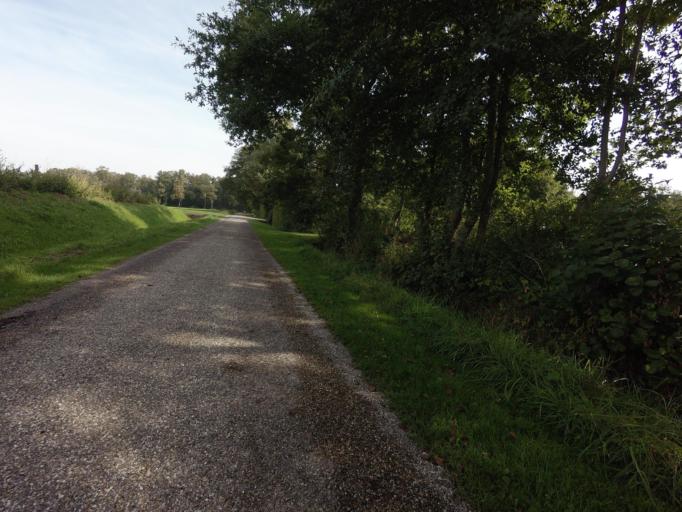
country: NL
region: Overijssel
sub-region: Gemeente Enschede
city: Enschede
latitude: 52.1874
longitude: 6.9426
